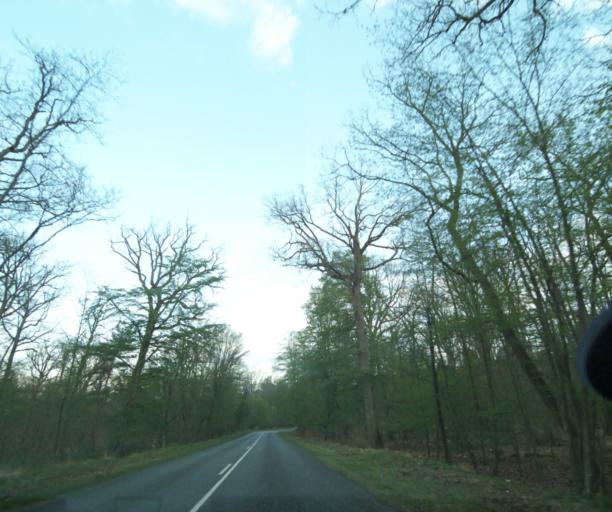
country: FR
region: Ile-de-France
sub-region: Departement de Seine-et-Marne
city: Fontainebleau
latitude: 48.3910
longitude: 2.7078
